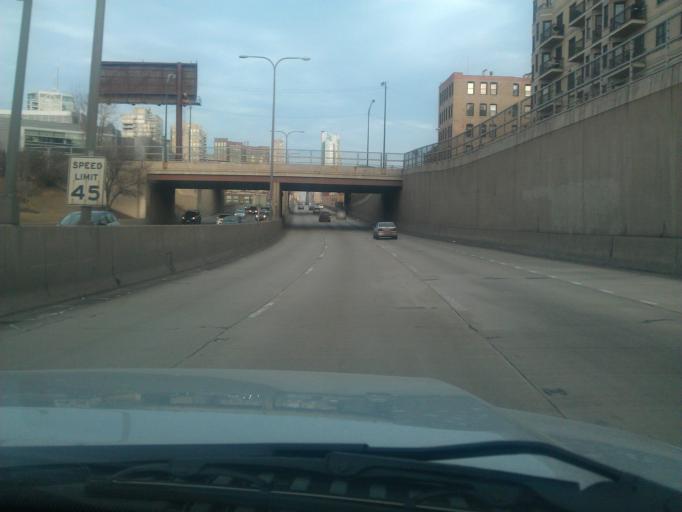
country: US
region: Illinois
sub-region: Cook County
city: Chicago
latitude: 41.8924
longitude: -87.6490
